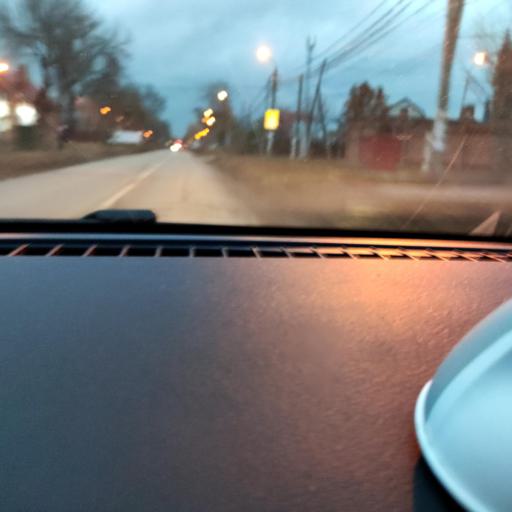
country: RU
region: Samara
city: Smyshlyayevka
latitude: 53.2445
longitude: 50.3375
